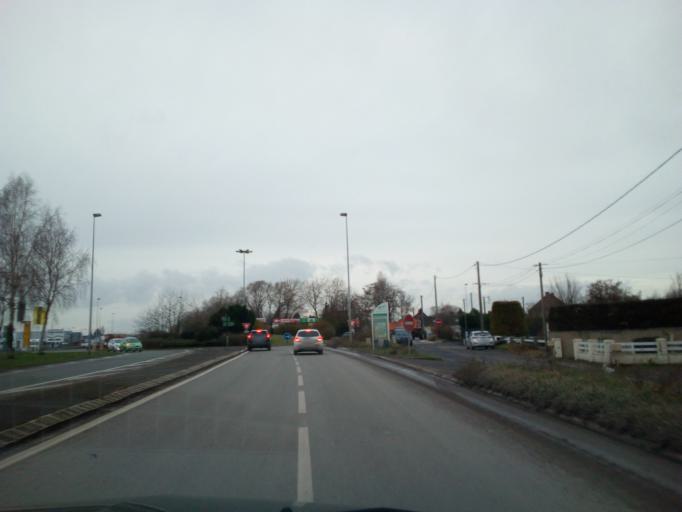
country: FR
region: Nord-Pas-de-Calais
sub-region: Departement du Pas-de-Calais
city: Beuvry
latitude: 50.5139
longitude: 2.6945
